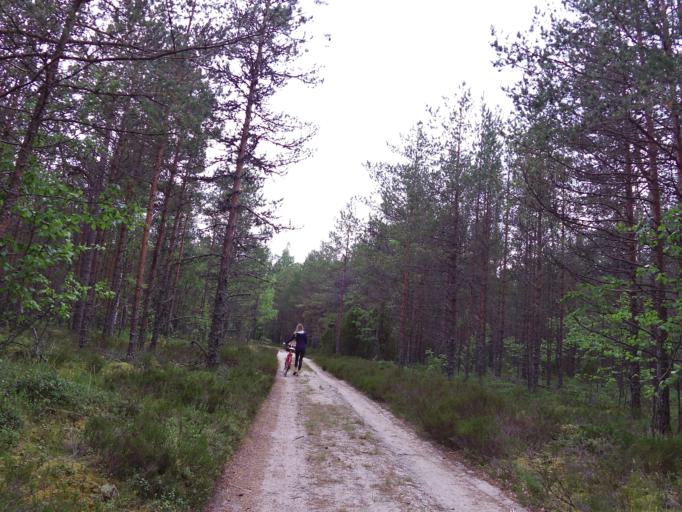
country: EE
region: Harju
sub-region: Paldiski linn
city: Paldiski
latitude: 59.2421
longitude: 23.7456
